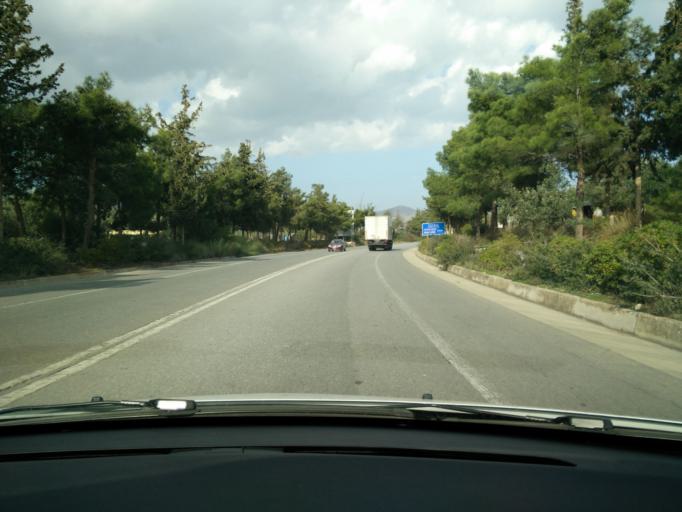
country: GR
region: Crete
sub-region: Nomos Lasithiou
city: Agios Nikolaos
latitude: 35.1932
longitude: 25.7027
